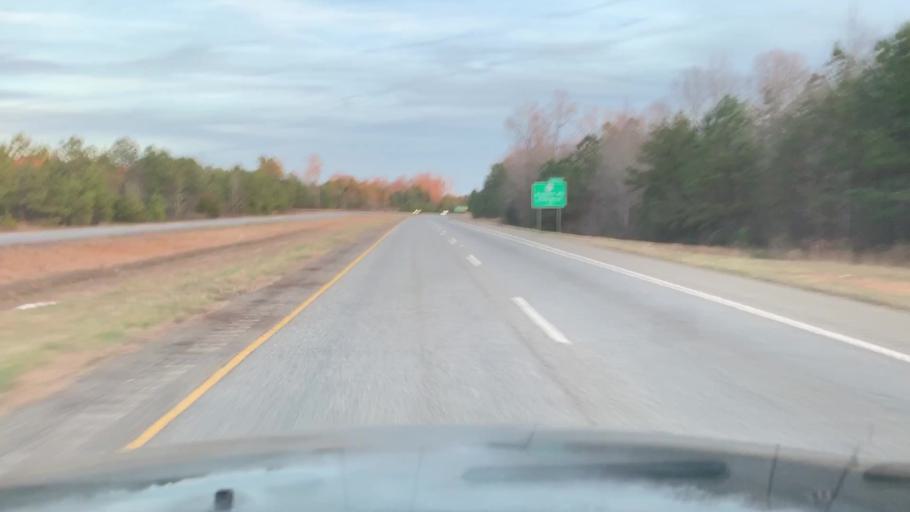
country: US
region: South Carolina
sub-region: Greenville County
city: Golden Grove
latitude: 34.7292
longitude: -82.4109
